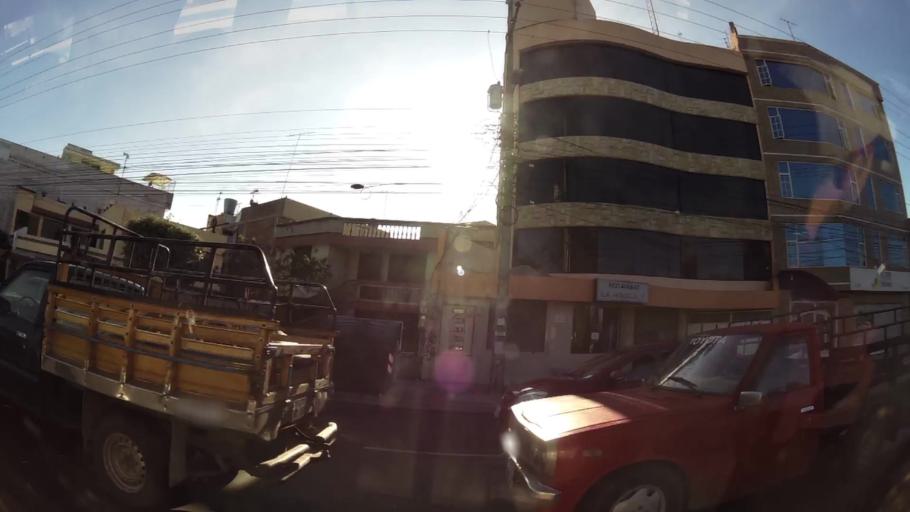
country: EC
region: Chimborazo
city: Riobamba
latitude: -1.6565
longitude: -78.6453
